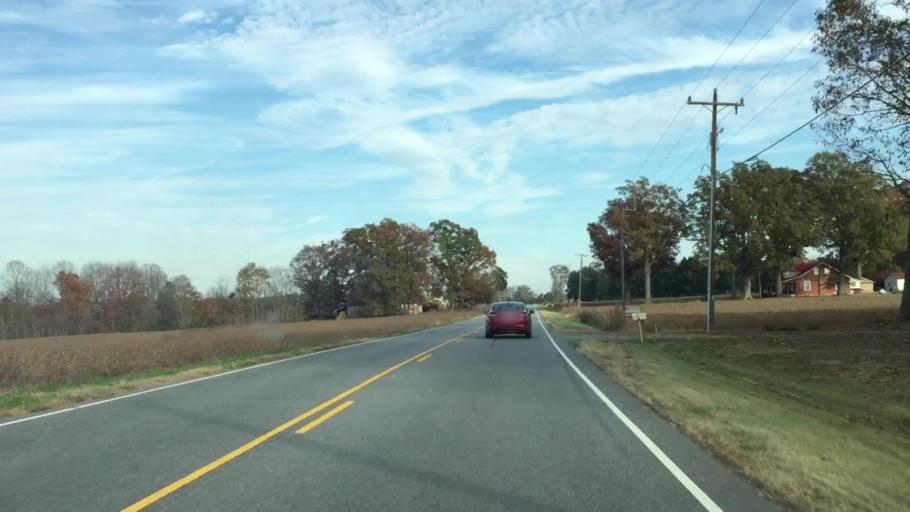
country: US
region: North Carolina
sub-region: Rockingham County
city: Reidsville
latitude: 36.2888
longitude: -79.7452
